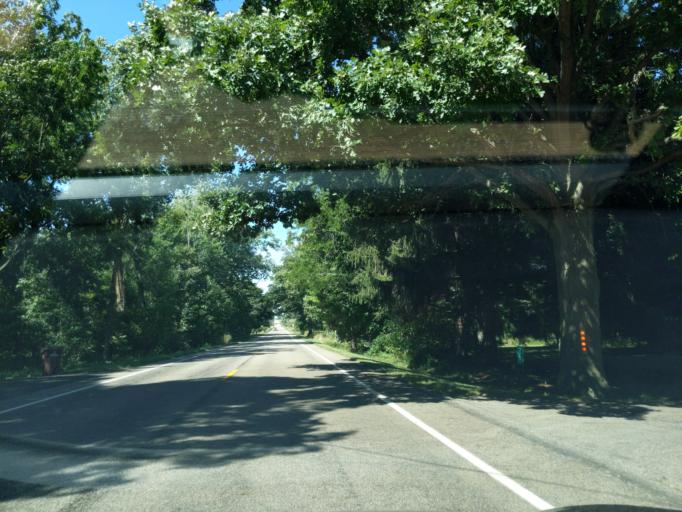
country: US
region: Michigan
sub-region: Eaton County
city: Potterville
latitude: 42.6259
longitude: -84.7707
